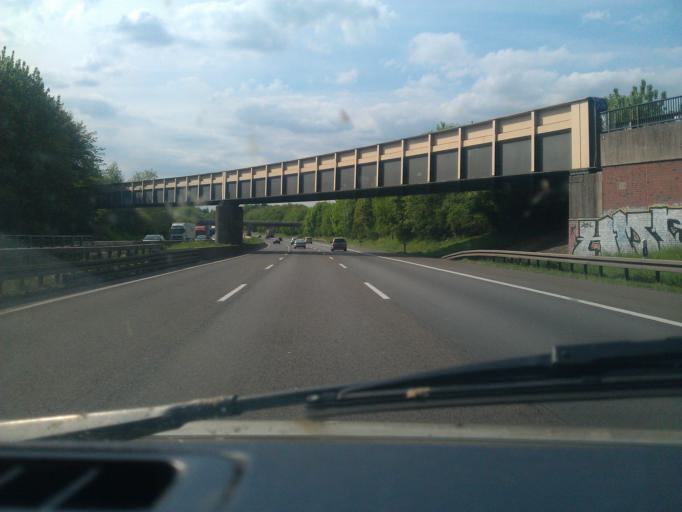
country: DE
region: North Rhine-Westphalia
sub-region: Regierungsbezirk Dusseldorf
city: Moers
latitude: 51.4892
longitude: 6.6550
